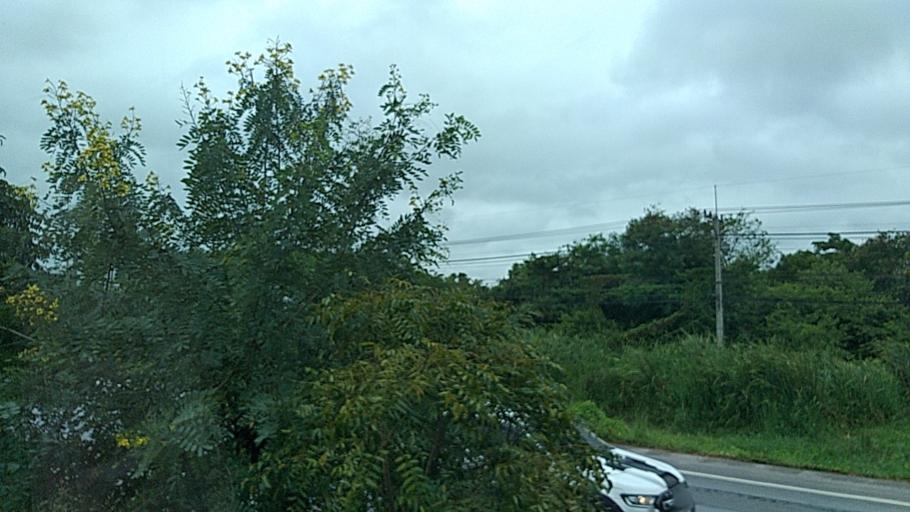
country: TH
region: Nakhon Ratchasima
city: Sida
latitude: 15.5439
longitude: 102.5472
